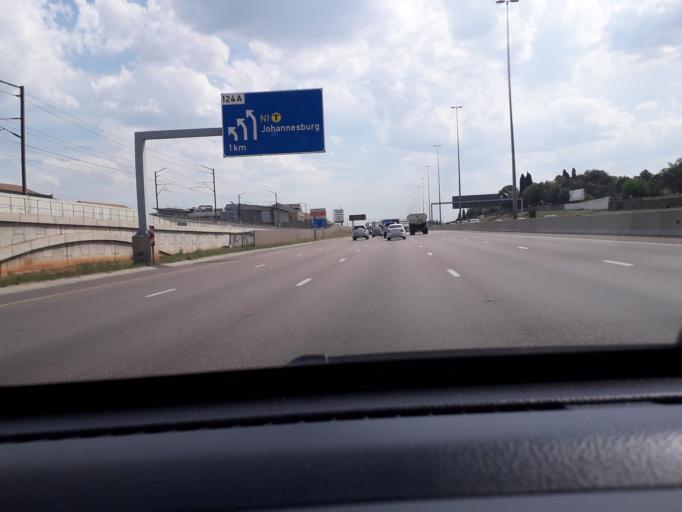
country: ZA
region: Gauteng
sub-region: City of Tshwane Metropolitan Municipality
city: Centurion
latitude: -25.8706
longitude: 28.1854
